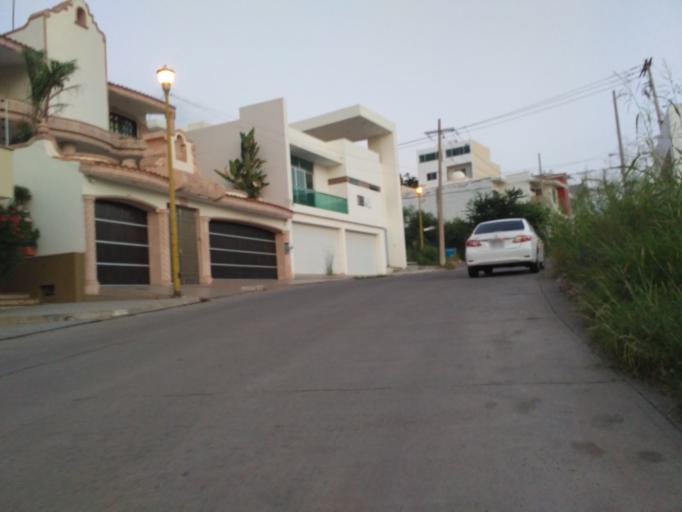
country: MX
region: Sinaloa
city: Culiacan
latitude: 24.7837
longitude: -107.3916
